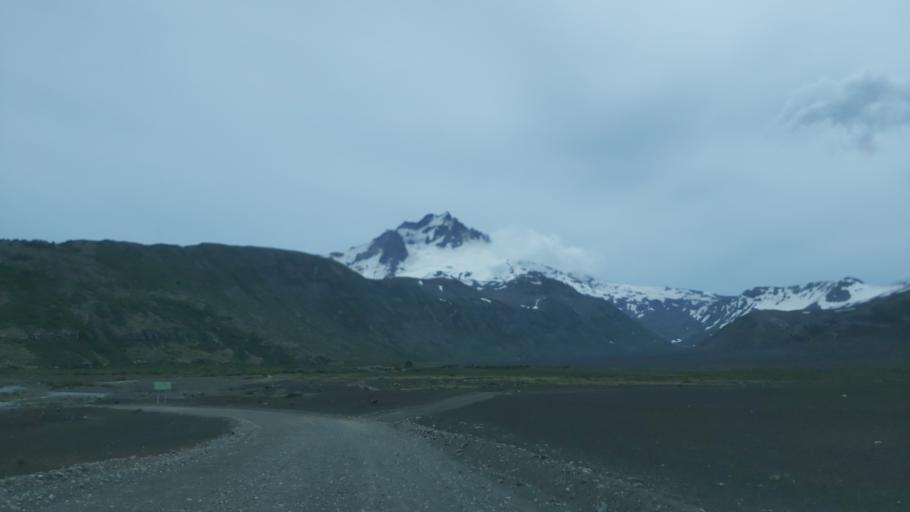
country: AR
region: Neuquen
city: Andacollo
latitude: -37.4613
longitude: -71.3119
